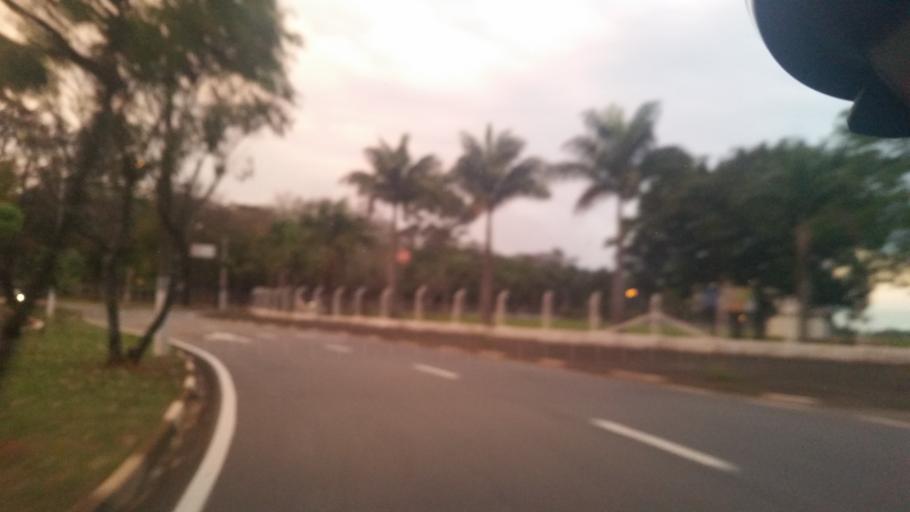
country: BR
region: Sao Paulo
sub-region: Campinas
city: Campinas
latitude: -22.8742
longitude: -47.0703
